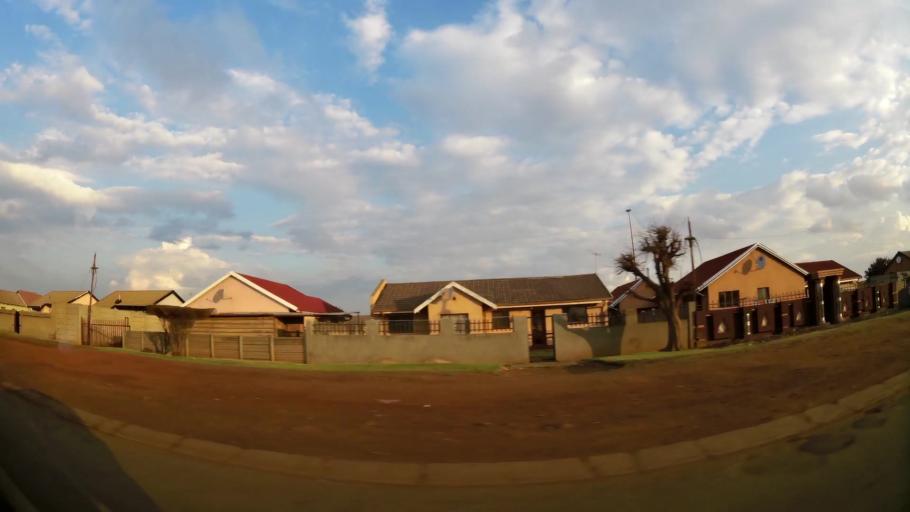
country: ZA
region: Gauteng
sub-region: City of Johannesburg Metropolitan Municipality
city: Orange Farm
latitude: -26.5935
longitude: 27.8406
